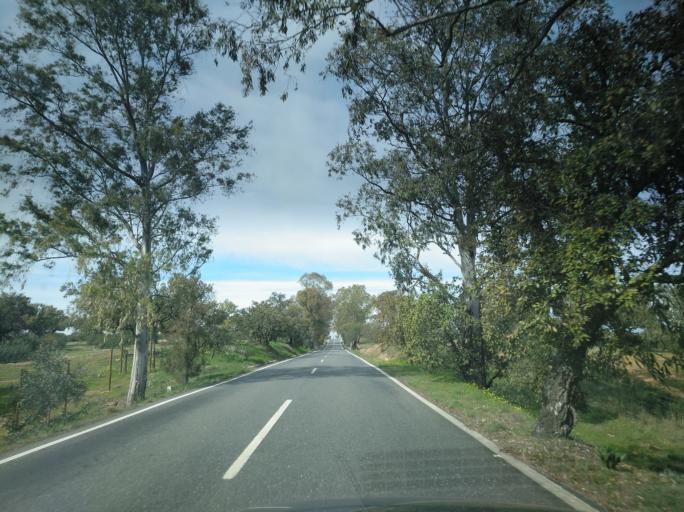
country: PT
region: Beja
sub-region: Mertola
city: Mertola
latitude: 37.7336
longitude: -7.7709
